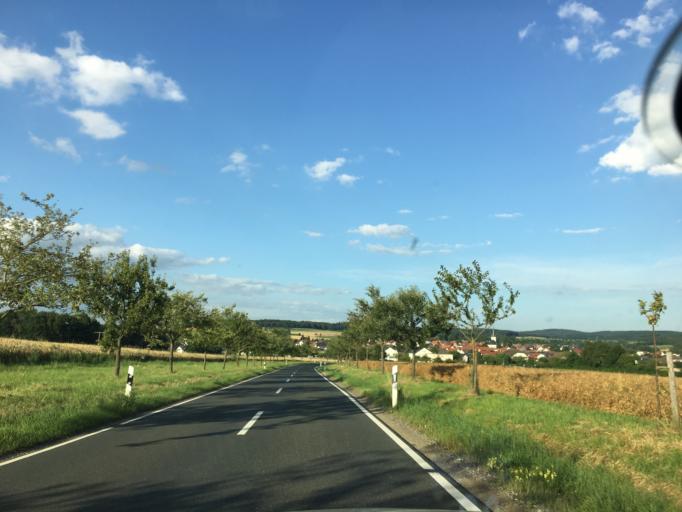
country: DE
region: Hesse
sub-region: Regierungsbezirk Darmstadt
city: Wehrheim
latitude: 50.3012
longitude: 8.5580
